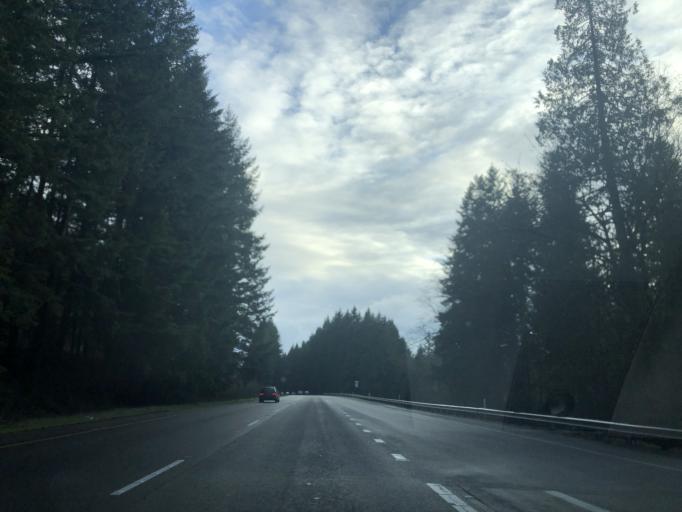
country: US
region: Washington
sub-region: Kitsap County
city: Bethel
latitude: 47.4640
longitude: -122.6243
